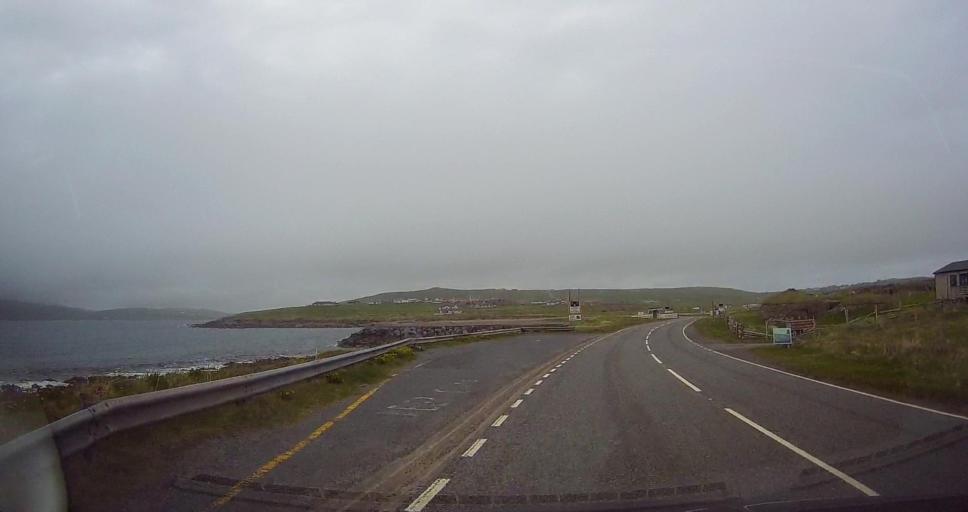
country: GB
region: Scotland
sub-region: Shetland Islands
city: Sandwick
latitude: 59.8784
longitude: -1.3069
